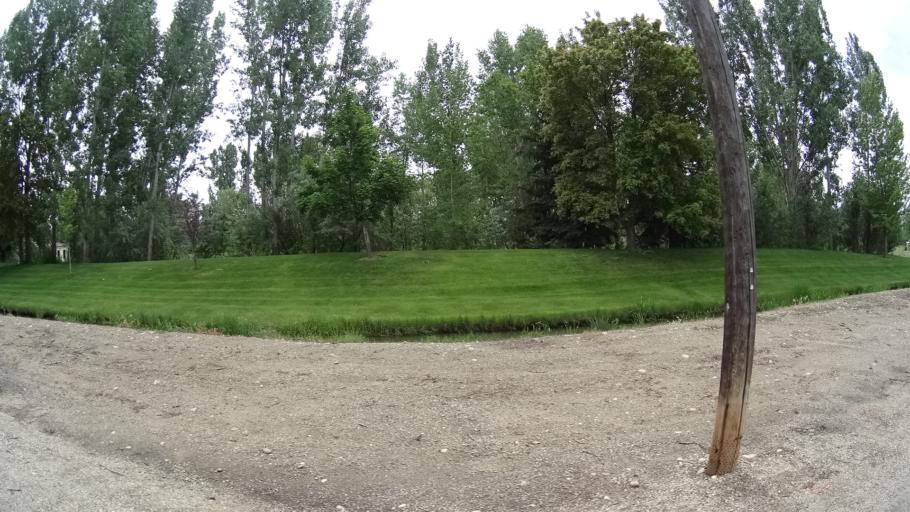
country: US
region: Idaho
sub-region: Ada County
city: Star
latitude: 43.6904
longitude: -116.4326
